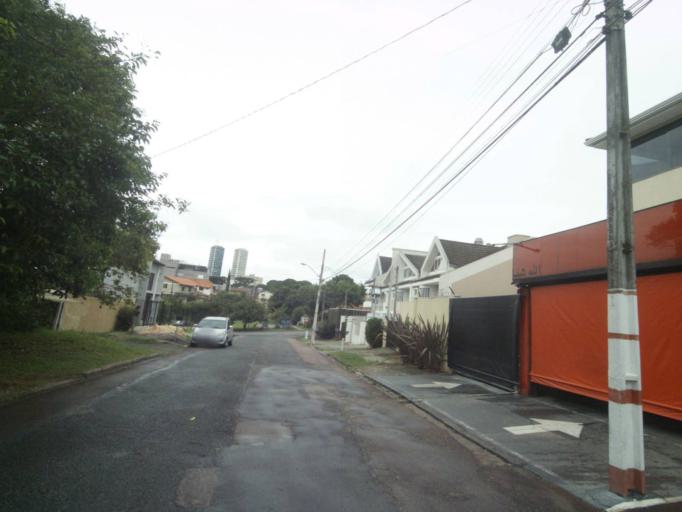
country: BR
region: Parana
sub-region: Curitiba
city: Curitiba
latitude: -25.4169
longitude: -49.2851
